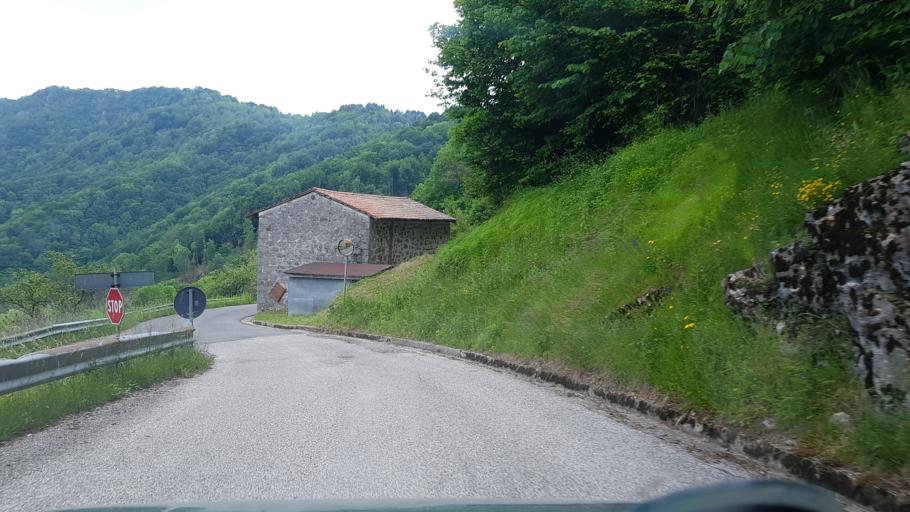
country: IT
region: Friuli Venezia Giulia
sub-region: Provincia di Udine
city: Pulfero
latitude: 46.1826
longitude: 13.4446
